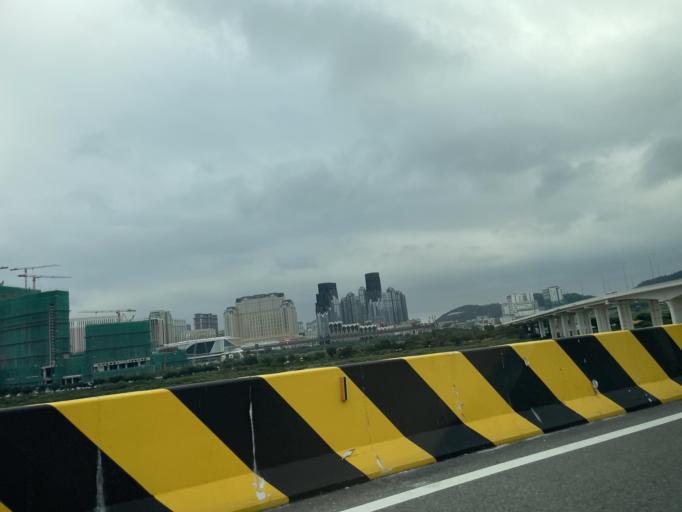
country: MO
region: Macau
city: Macau
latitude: 22.1414
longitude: 113.5477
